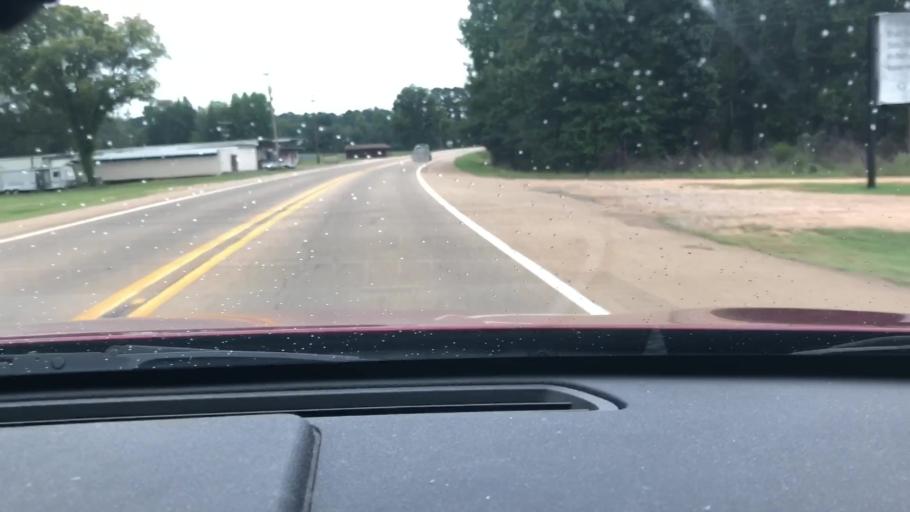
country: US
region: Arkansas
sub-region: Lafayette County
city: Stamps
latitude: 33.3676
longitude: -93.5150
